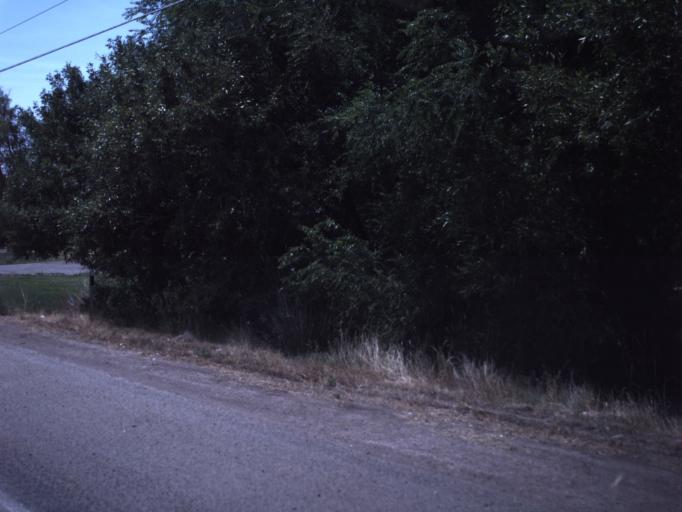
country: US
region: Utah
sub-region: Uintah County
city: Vernal
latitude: 40.4721
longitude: -109.5289
